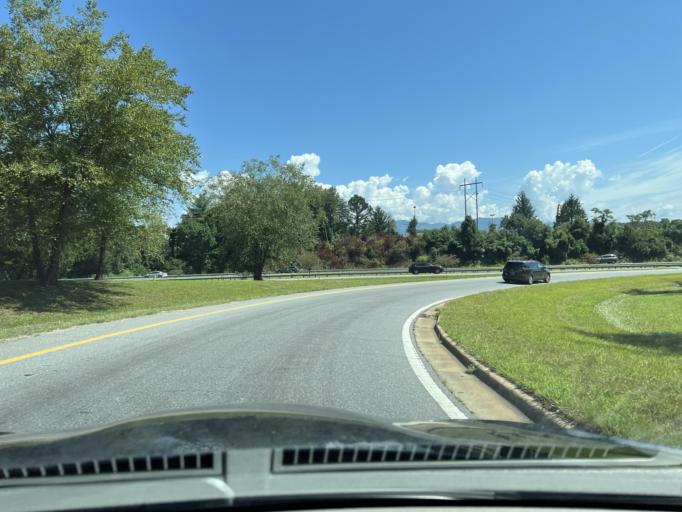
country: US
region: North Carolina
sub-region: Buncombe County
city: Biltmore Forest
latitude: 35.5684
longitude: -82.5098
